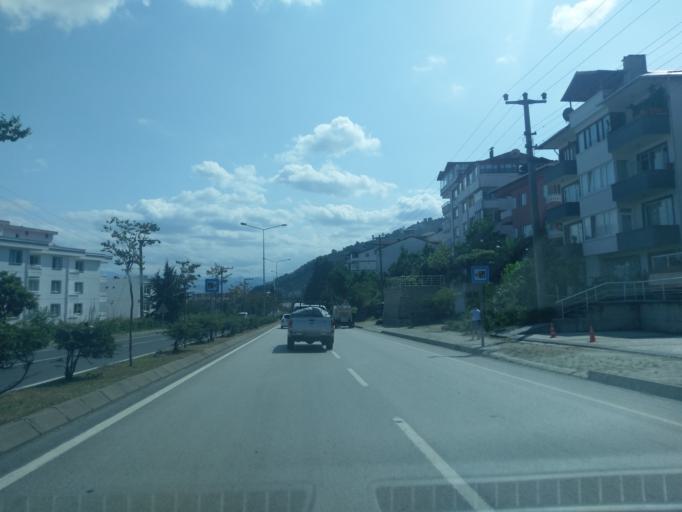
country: TR
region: Ordu
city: Ordu
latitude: 41.0081
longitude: 37.8689
